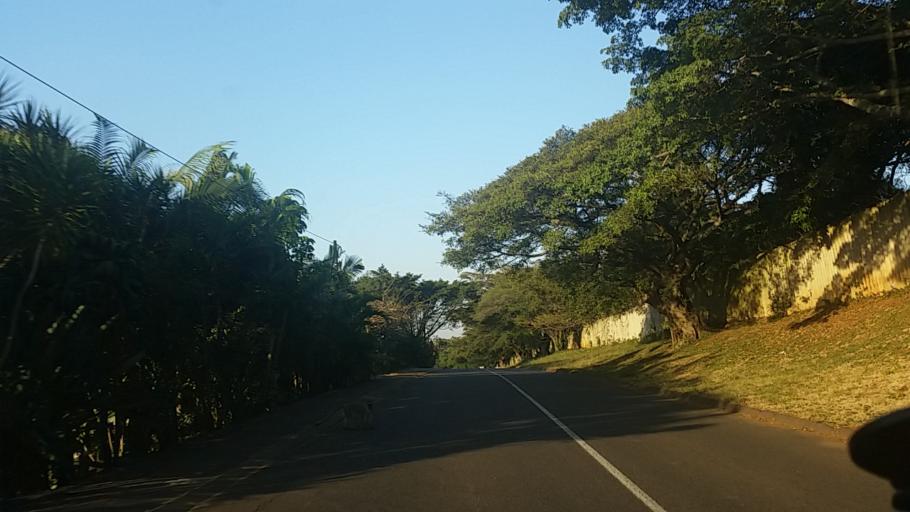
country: ZA
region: KwaZulu-Natal
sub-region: eThekwini Metropolitan Municipality
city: Berea
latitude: -29.8533
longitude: 30.9140
